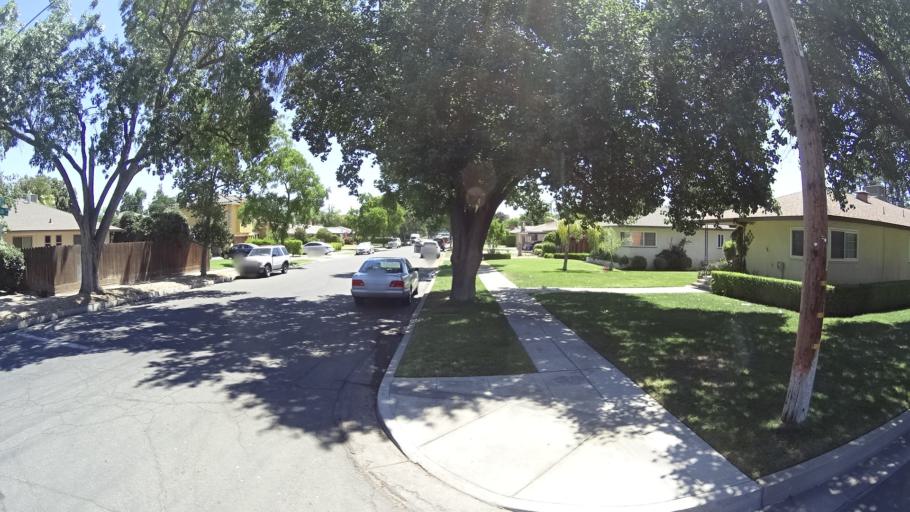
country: US
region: California
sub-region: Fresno County
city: Fresno
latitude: 36.7857
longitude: -119.8130
